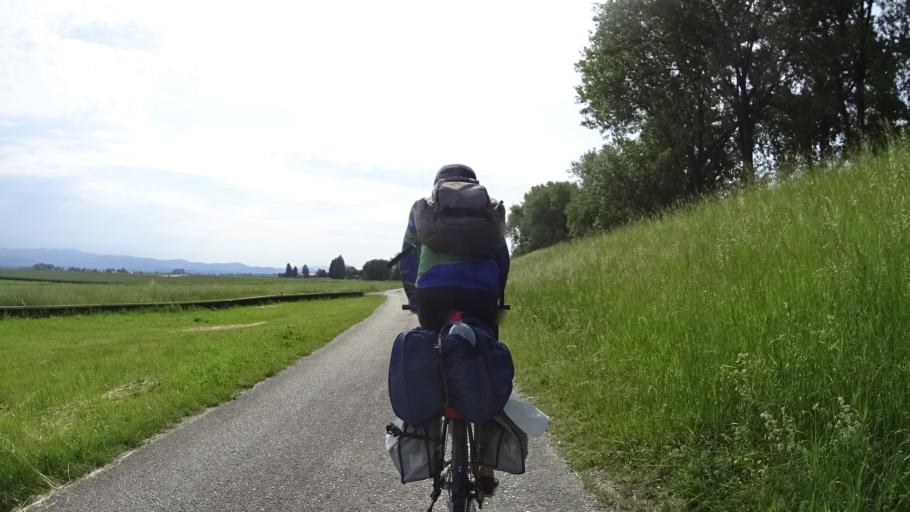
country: DE
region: Bavaria
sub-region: Lower Bavaria
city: Mariaposching
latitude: 48.8284
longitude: 12.7960
